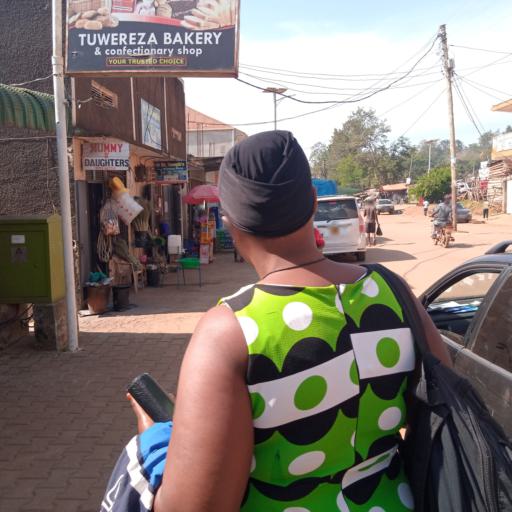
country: UG
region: Central Region
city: Masaka
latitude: -0.3471
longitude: 31.7394
